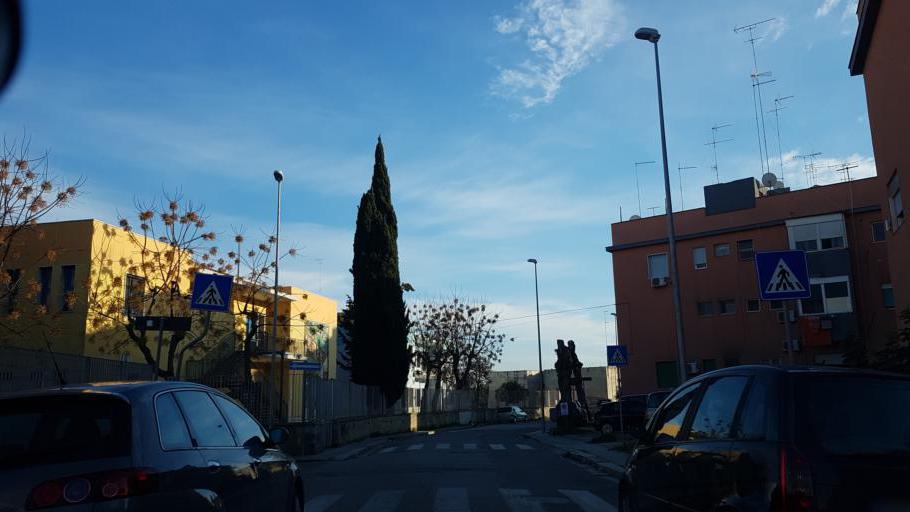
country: IT
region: Apulia
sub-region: Provincia di Brindisi
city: Brindisi
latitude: 40.6262
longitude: 17.9338
